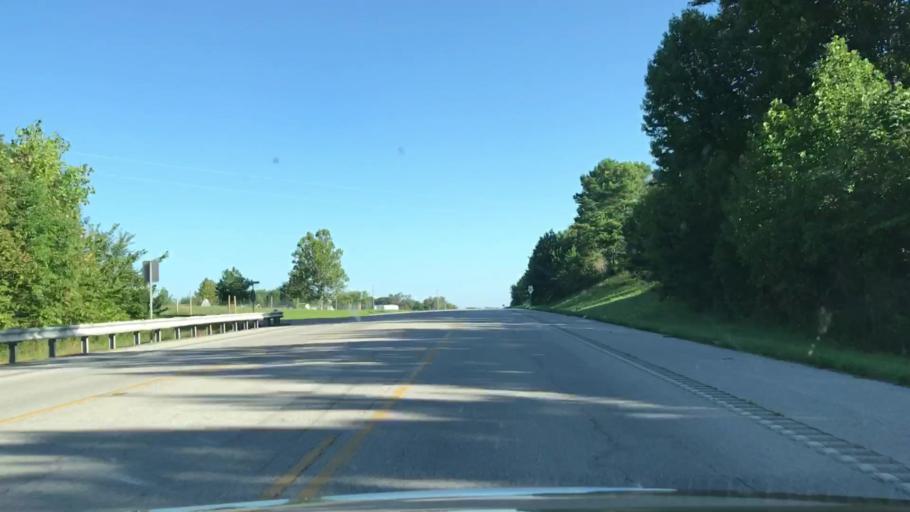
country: US
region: Tennessee
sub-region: Putnam County
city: Baxter
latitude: 36.2243
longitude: -85.6163
